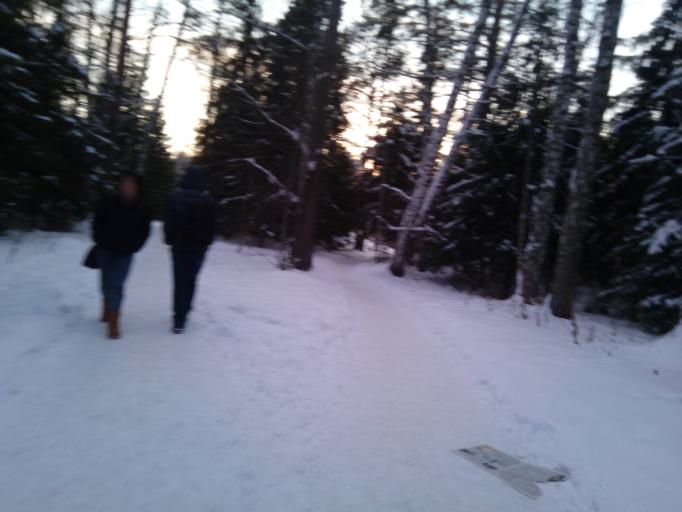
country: RU
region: Novosibirsk
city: Akademgorodok
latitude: 54.8403
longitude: 83.0889
